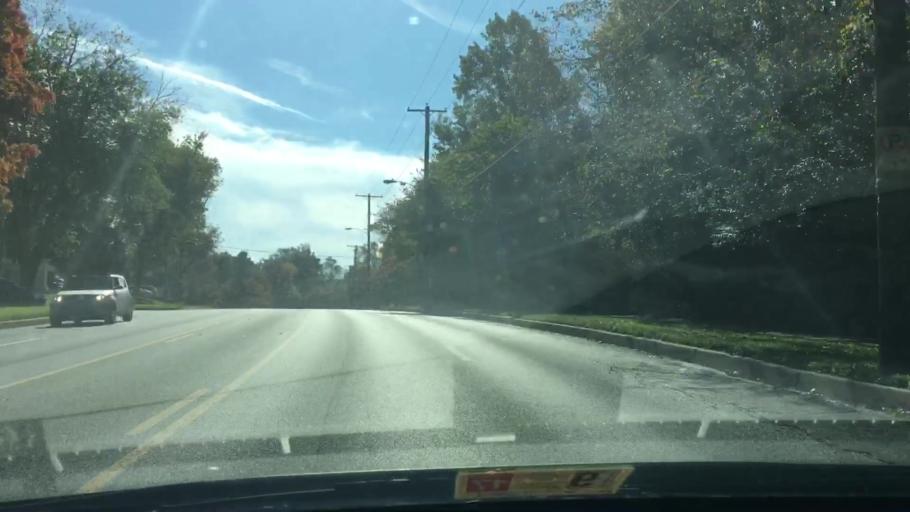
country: US
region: Maryland
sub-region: Montgomery County
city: North Bethesda
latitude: 39.0706
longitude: -77.1140
